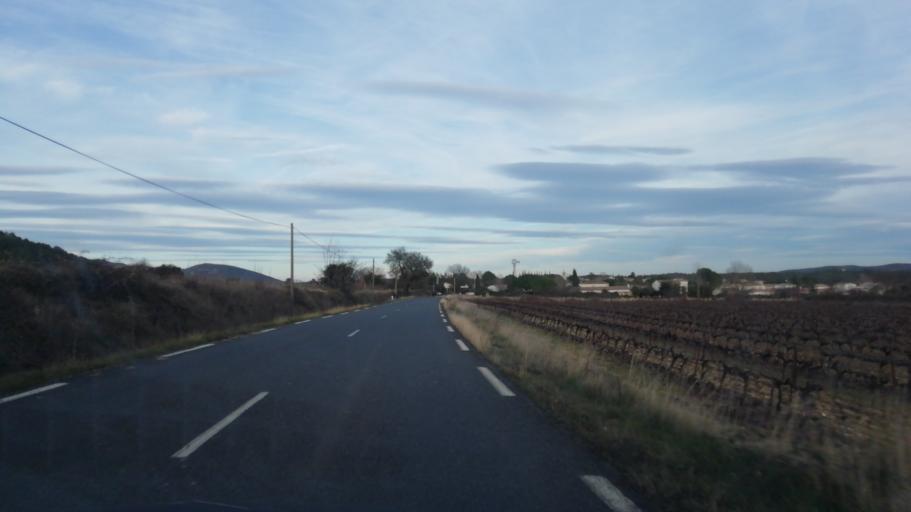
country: FR
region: Languedoc-Roussillon
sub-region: Departement de l'Herault
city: Claret
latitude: 43.8398
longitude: 3.9353
